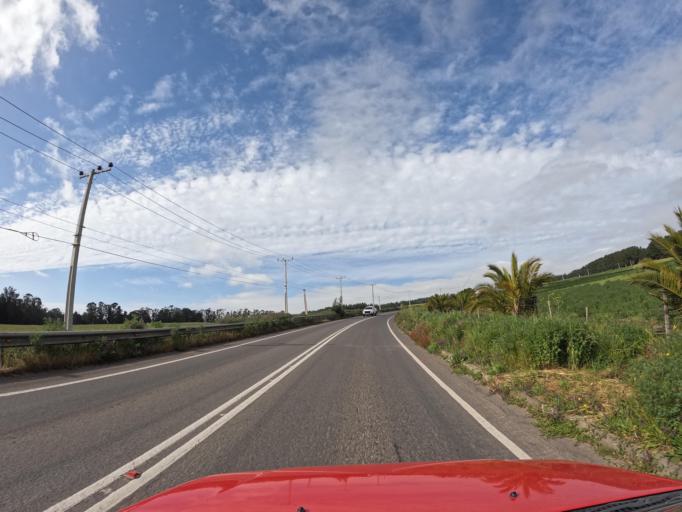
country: CL
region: O'Higgins
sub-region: Provincia de Colchagua
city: Santa Cruz
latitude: -34.3677
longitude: -71.9642
